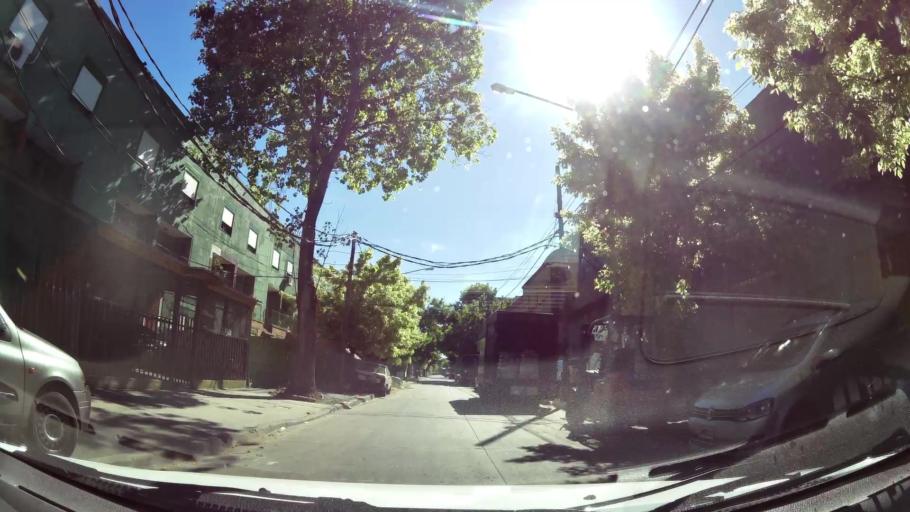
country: AR
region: Buenos Aires
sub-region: Partido de General San Martin
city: General San Martin
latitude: -34.5485
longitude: -58.5206
